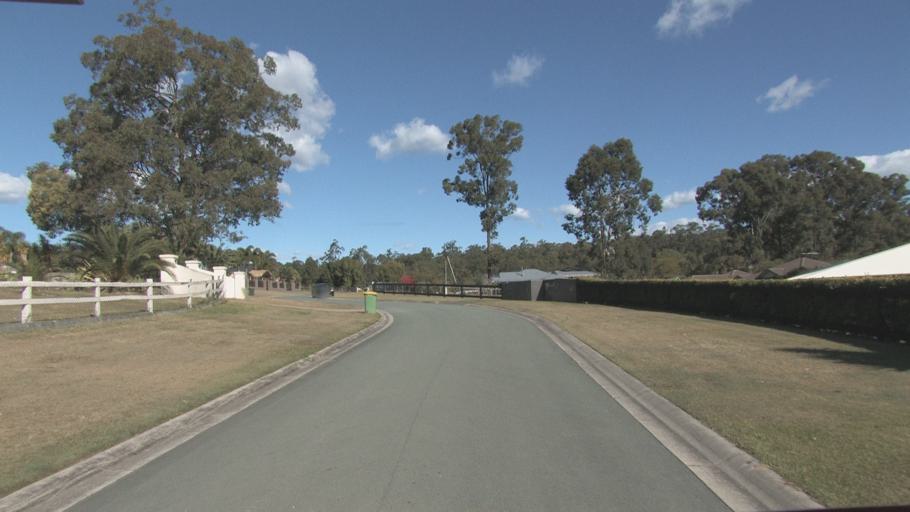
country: AU
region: Queensland
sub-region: Ipswich
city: Springfield Lakes
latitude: -27.7327
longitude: 152.9089
